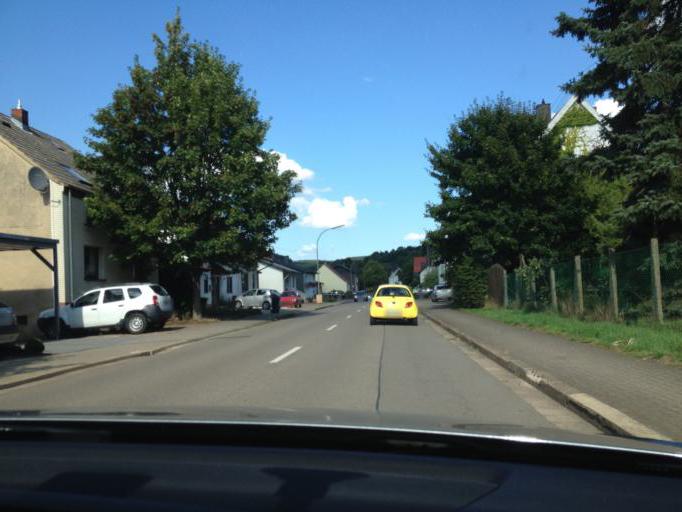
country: DE
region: Saarland
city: Illingen
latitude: 49.3935
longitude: 7.0369
